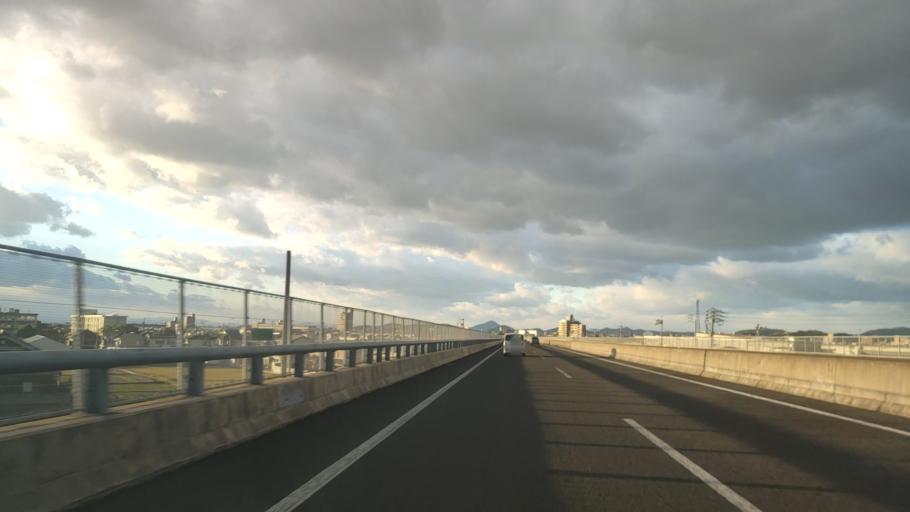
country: JP
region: Ehime
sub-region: Shikoku-chuo Shi
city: Matsuyama
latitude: 33.7921
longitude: 132.8022
